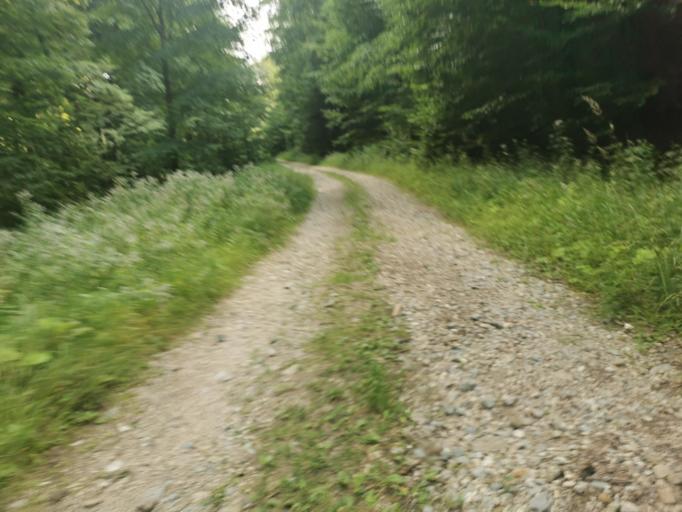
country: SK
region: Trenciansky
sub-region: Okres Myjava
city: Myjava
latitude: 48.8177
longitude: 17.6141
